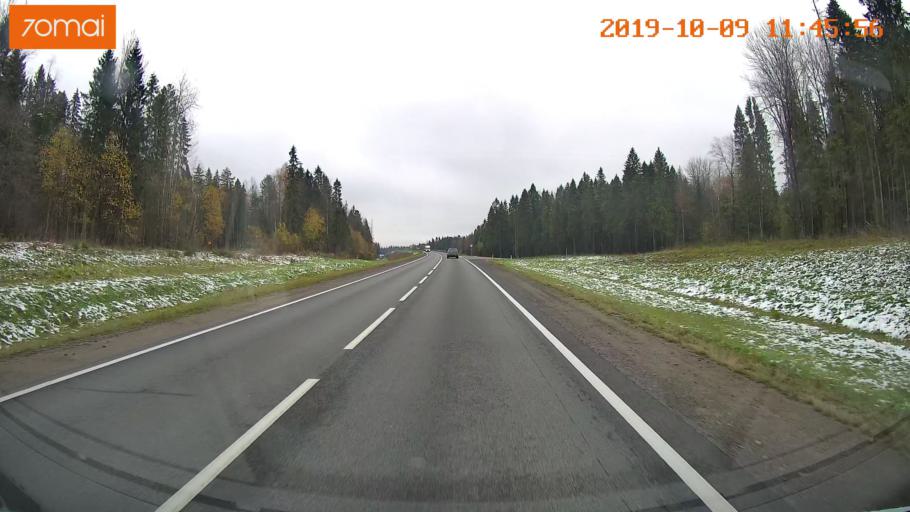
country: RU
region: Vologda
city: Gryazovets
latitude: 58.8613
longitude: 40.1987
